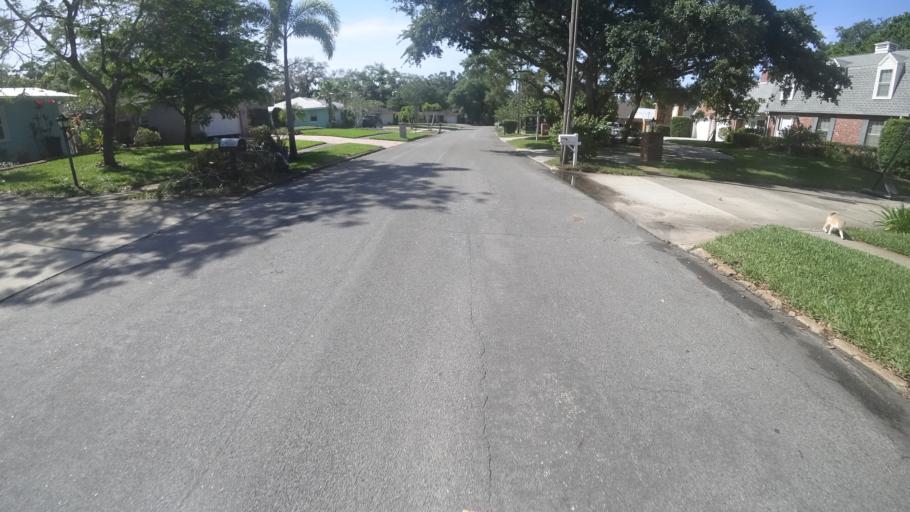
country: US
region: Florida
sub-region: Manatee County
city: West Bradenton
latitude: 27.5044
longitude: -82.6178
